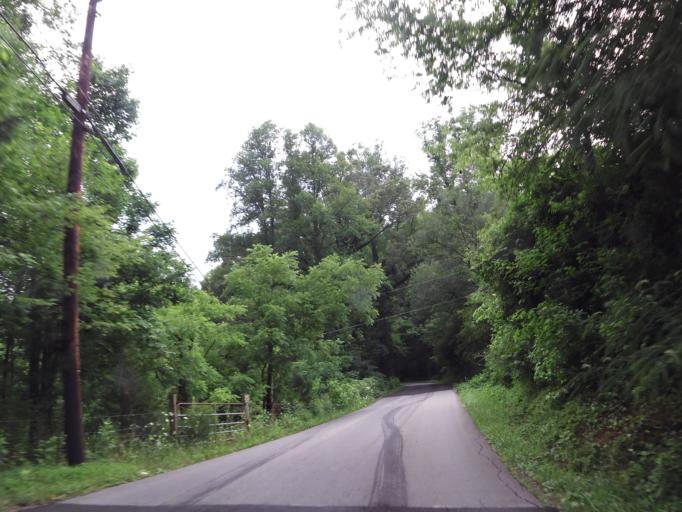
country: US
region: Tennessee
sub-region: Blount County
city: Wildwood
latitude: 35.7387
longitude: -83.7999
